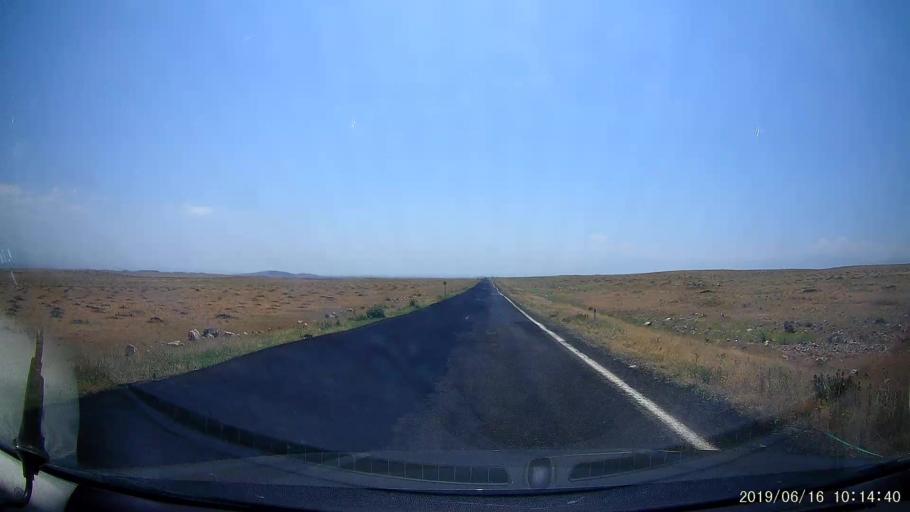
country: TR
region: Igdir
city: Tuzluca
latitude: 40.1830
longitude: 43.6672
